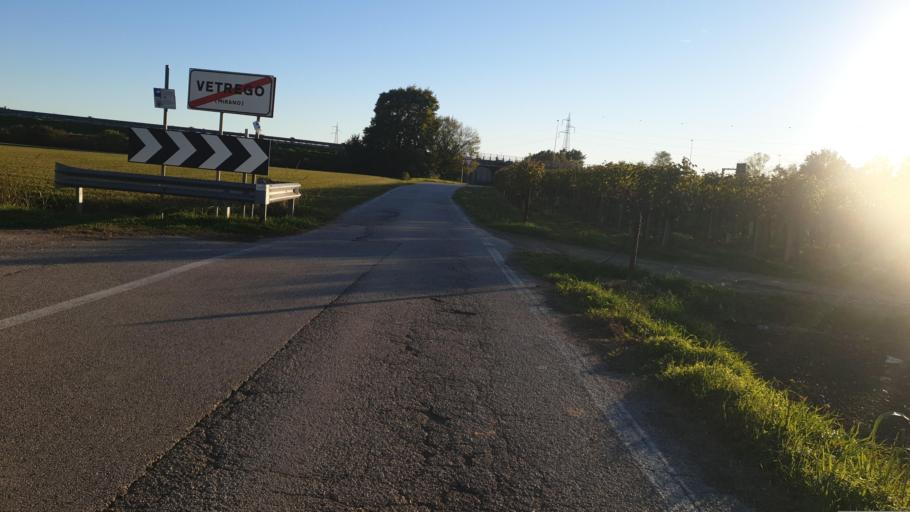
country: IT
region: Veneto
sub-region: Provincia di Venezia
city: Marano
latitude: 45.4528
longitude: 12.1001
